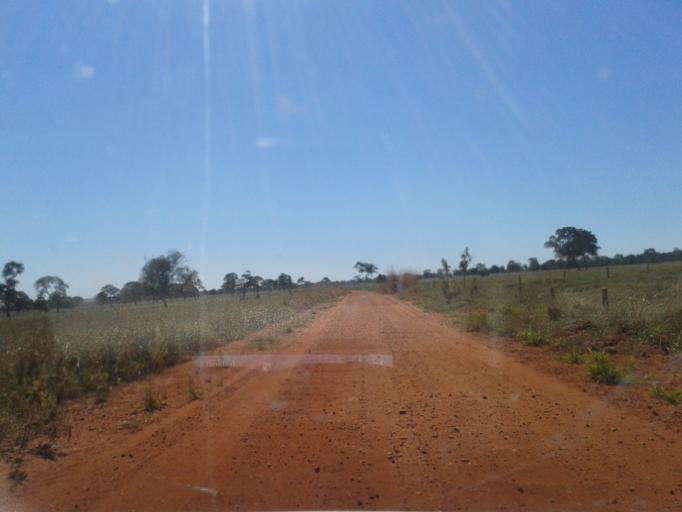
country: BR
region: Minas Gerais
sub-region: Santa Vitoria
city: Santa Vitoria
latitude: -19.0751
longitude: -50.3593
